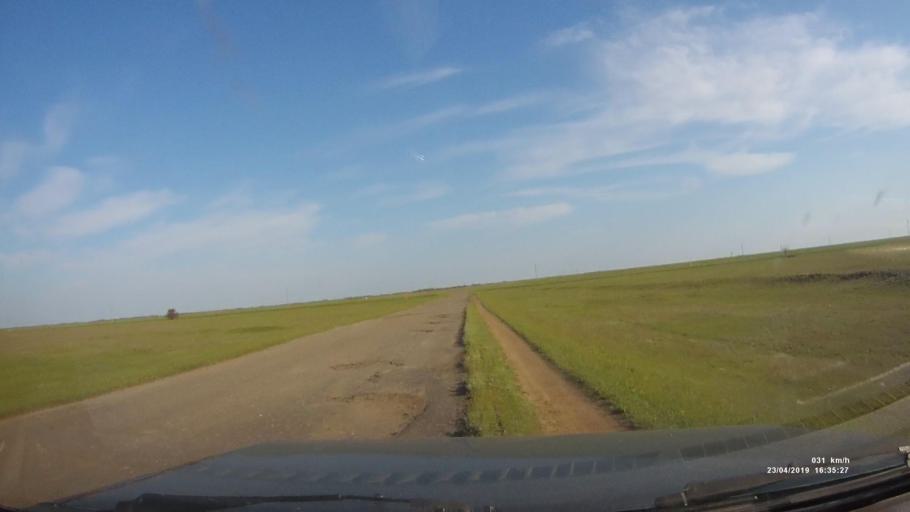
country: RU
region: Kalmykiya
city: Priyutnoye
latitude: 46.3308
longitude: 43.1375
